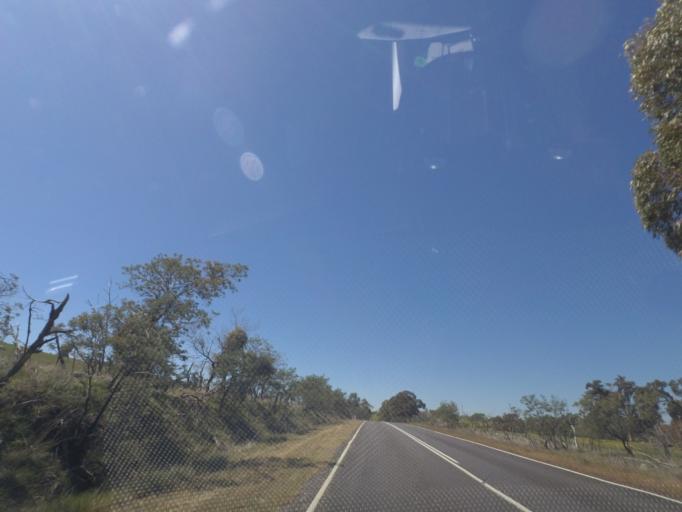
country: AU
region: Victoria
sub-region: Hume
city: Sunbury
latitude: -37.1668
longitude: 144.7581
